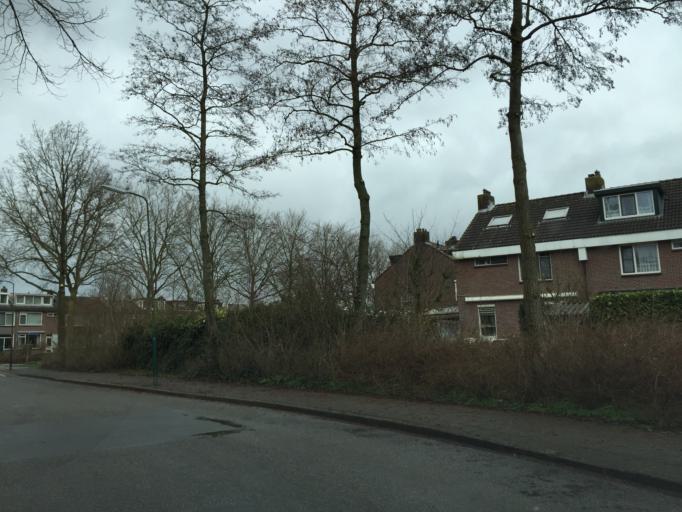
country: NL
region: Utrecht
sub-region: Gemeente Montfoort
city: Montfoort
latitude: 52.0859
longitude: 4.9577
